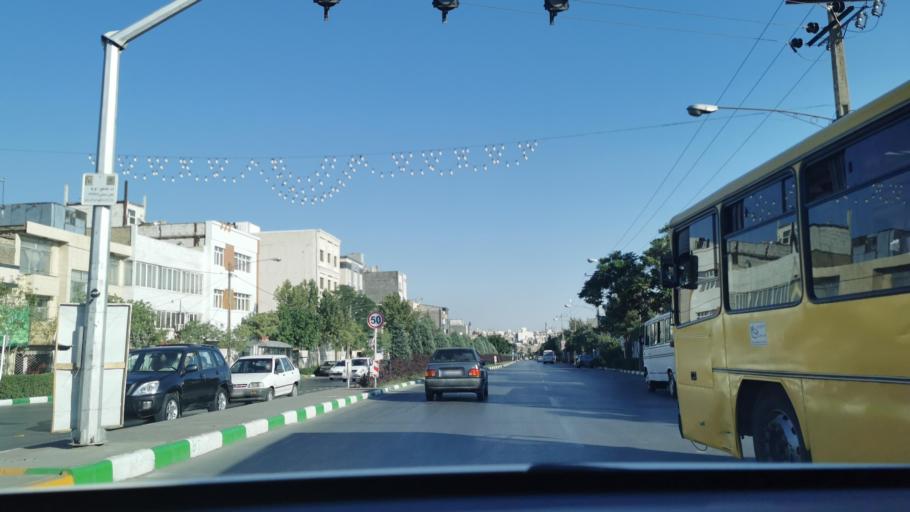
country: IR
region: Razavi Khorasan
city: Mashhad
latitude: 36.3071
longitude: 59.5086
